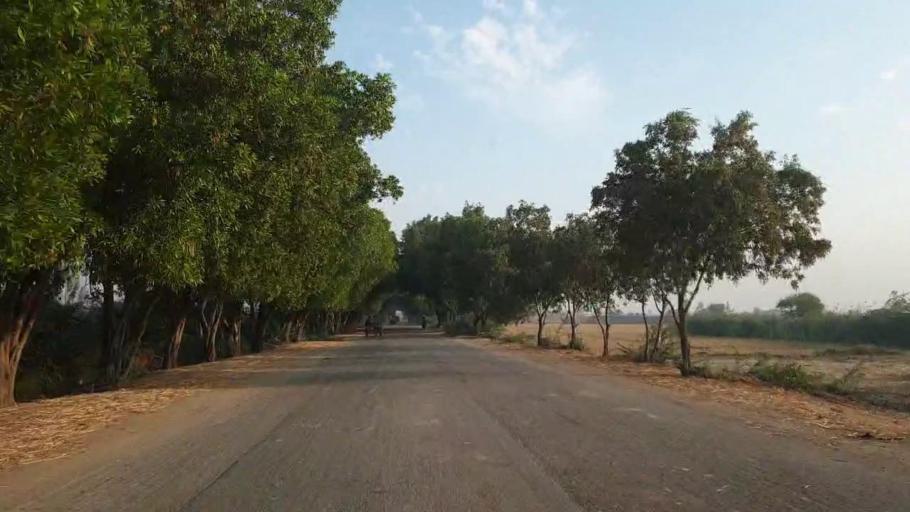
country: PK
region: Sindh
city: Tando Bago
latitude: 24.7715
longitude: 68.9589
